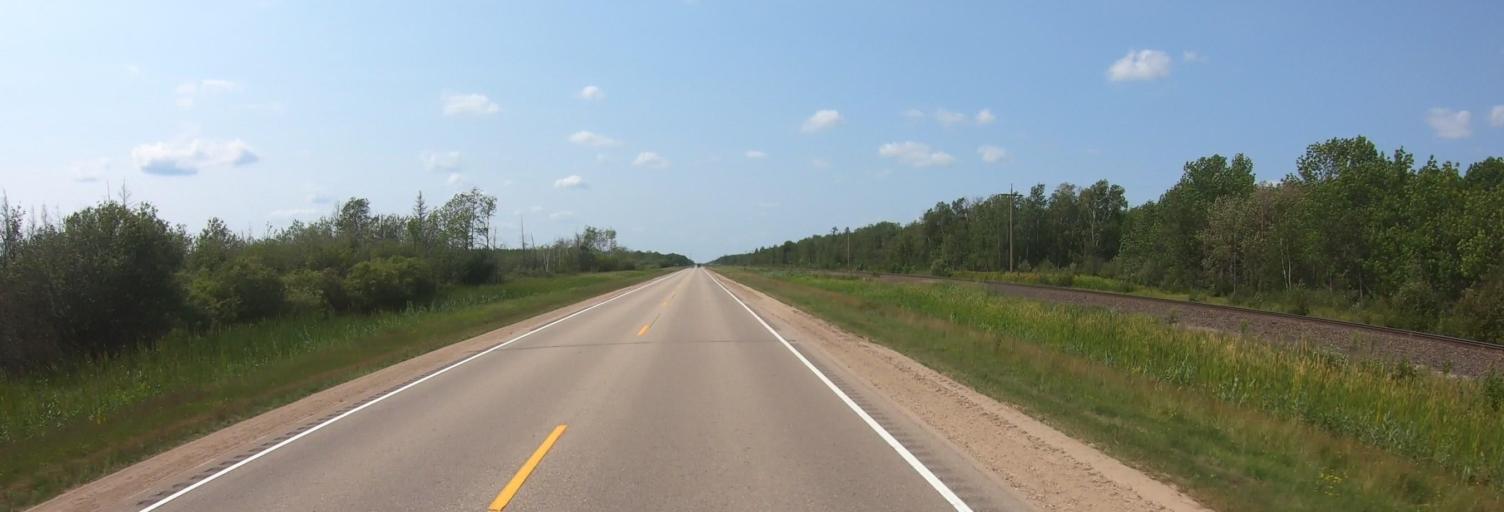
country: US
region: Minnesota
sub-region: Roseau County
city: Warroad
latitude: 48.7765
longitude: -94.9943
